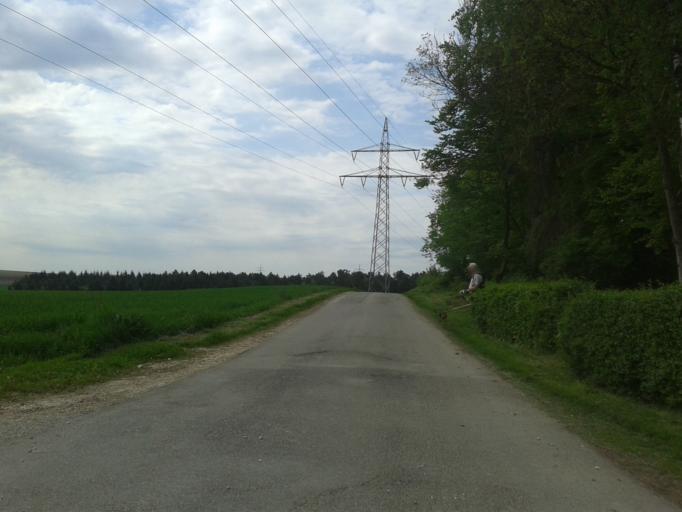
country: DE
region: Baden-Wuerttemberg
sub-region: Tuebingen Region
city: Blaubeuren
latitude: 48.3911
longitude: 9.7887
